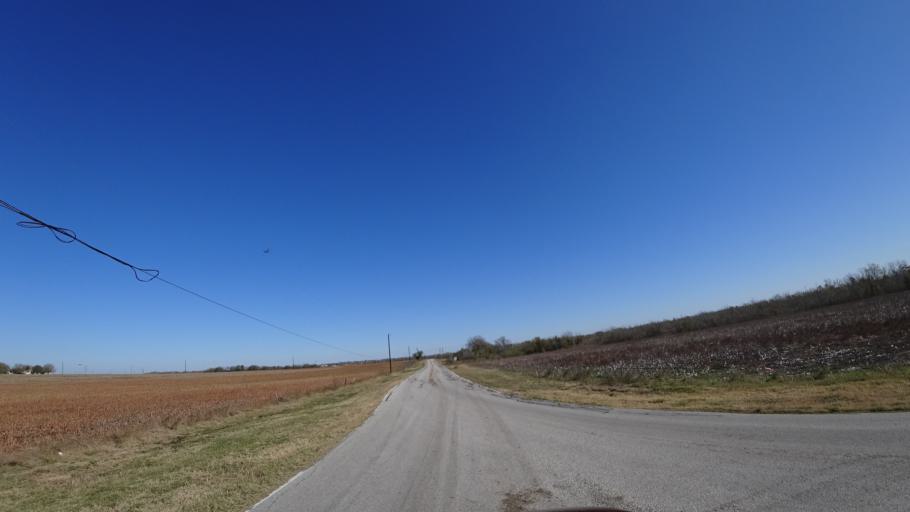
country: US
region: Texas
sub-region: Travis County
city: Onion Creek
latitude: 30.0957
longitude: -97.6601
